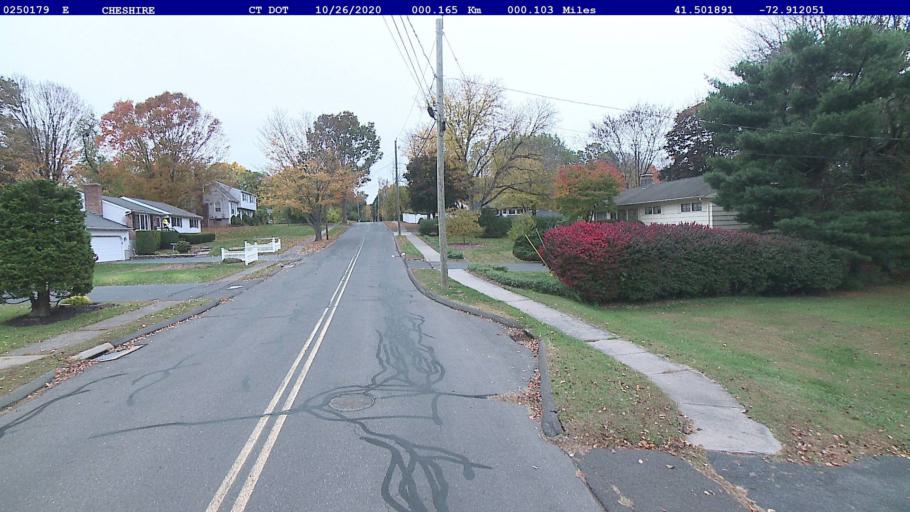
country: US
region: Connecticut
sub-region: New Haven County
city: Cheshire
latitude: 41.5019
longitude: -72.9120
